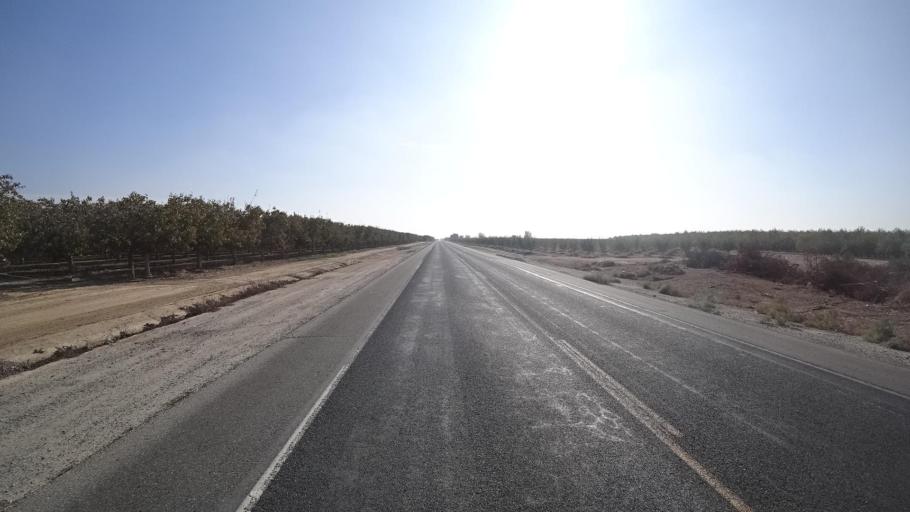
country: US
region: California
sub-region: Kern County
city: McFarland
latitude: 35.6576
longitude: -119.1957
